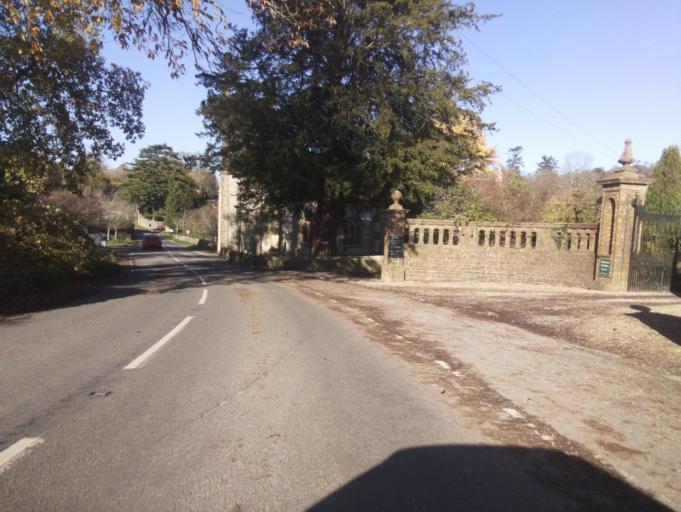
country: GB
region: England
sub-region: Dorset
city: Sherborne
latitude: 50.8372
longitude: -2.4847
